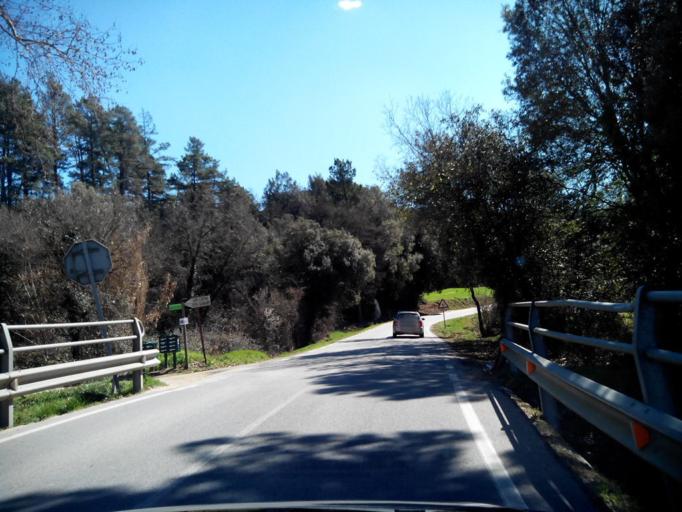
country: ES
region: Catalonia
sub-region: Provincia de Barcelona
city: Dosrius
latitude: 41.6013
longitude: 2.4223
